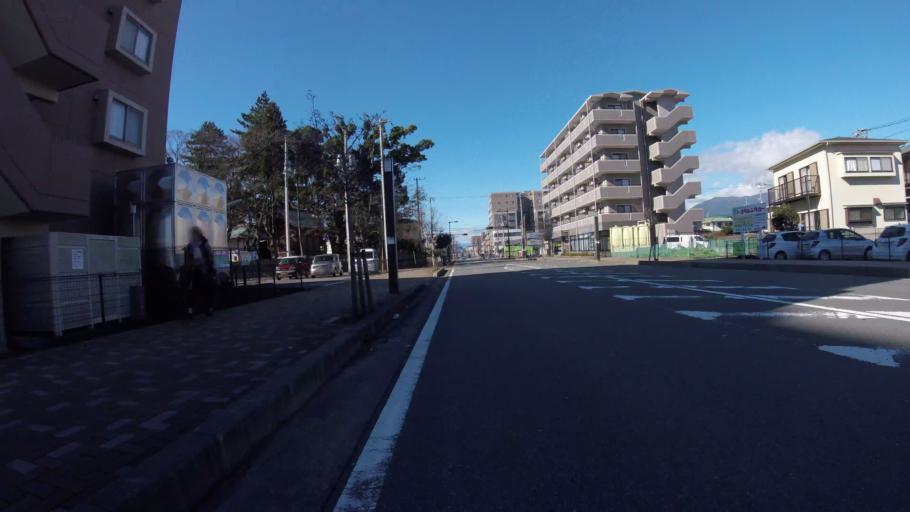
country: JP
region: Shizuoka
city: Mishima
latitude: 35.1288
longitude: 138.9032
